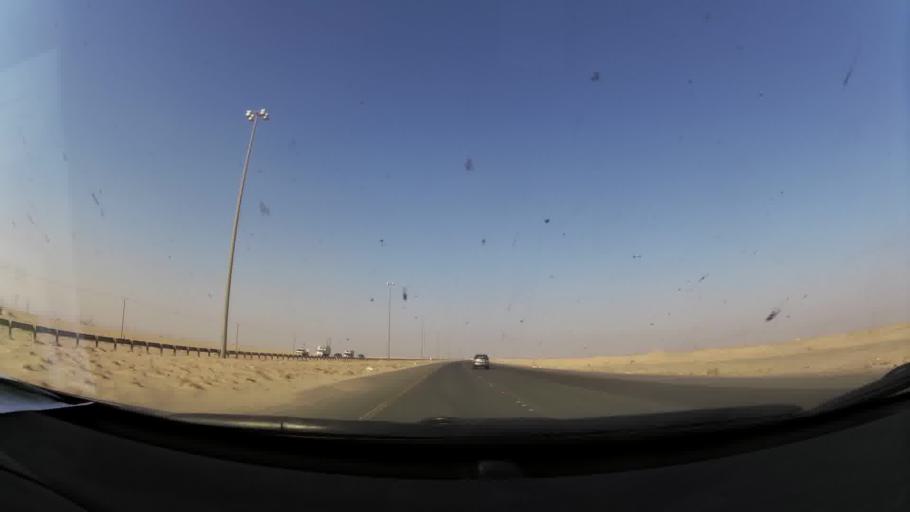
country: KW
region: Muhafazat al Jahra'
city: Al Jahra'
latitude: 29.6990
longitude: 47.6682
